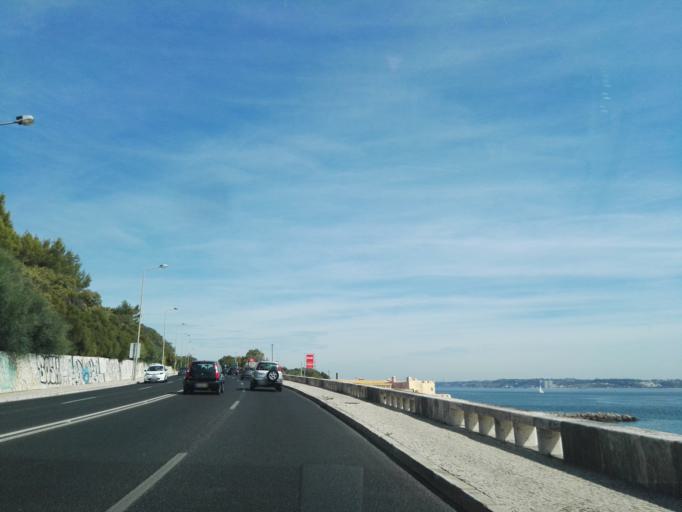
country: PT
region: Lisbon
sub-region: Oeiras
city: Oeiras
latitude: 38.6855
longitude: -9.3082
